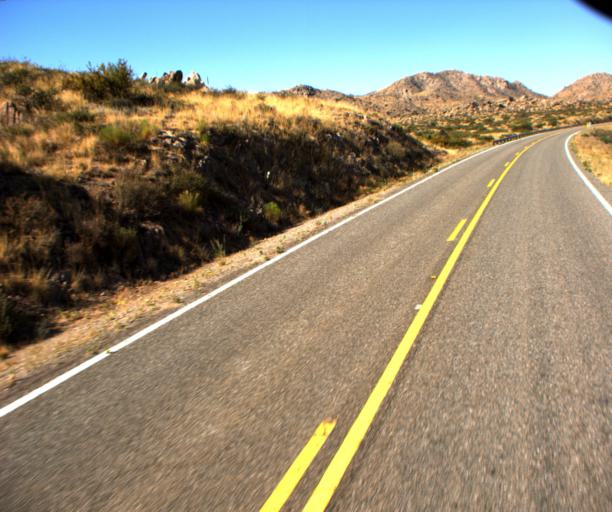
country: US
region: Arizona
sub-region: Graham County
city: Swift Trail Junction
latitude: 32.5676
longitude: -109.7209
